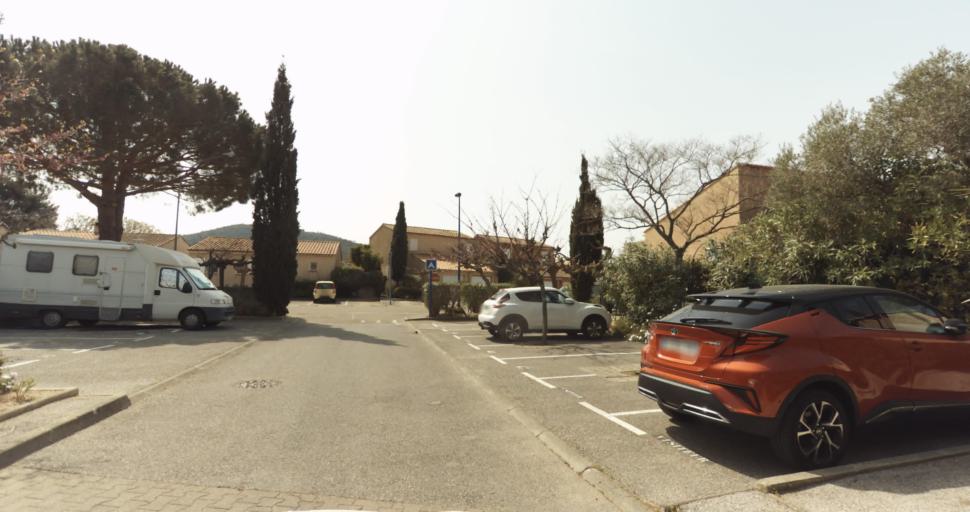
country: FR
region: Provence-Alpes-Cote d'Azur
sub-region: Departement du Var
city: Bormes-les-Mimosas
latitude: 43.1340
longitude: 6.3425
